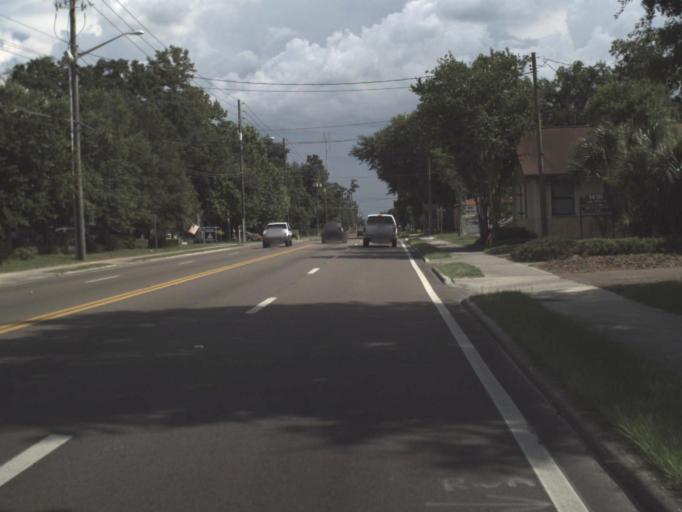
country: US
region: Florida
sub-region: Alachua County
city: Gainesville
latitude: 29.6656
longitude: -82.3309
